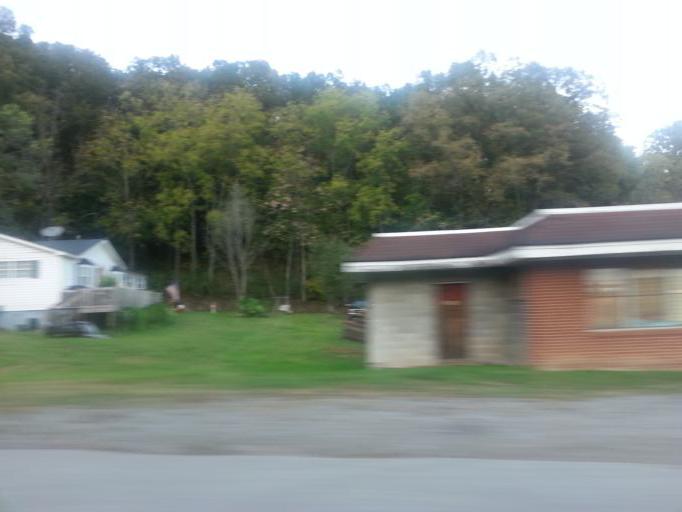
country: US
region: Tennessee
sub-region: Campbell County
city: Caryville
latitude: 36.2750
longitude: -84.2025
